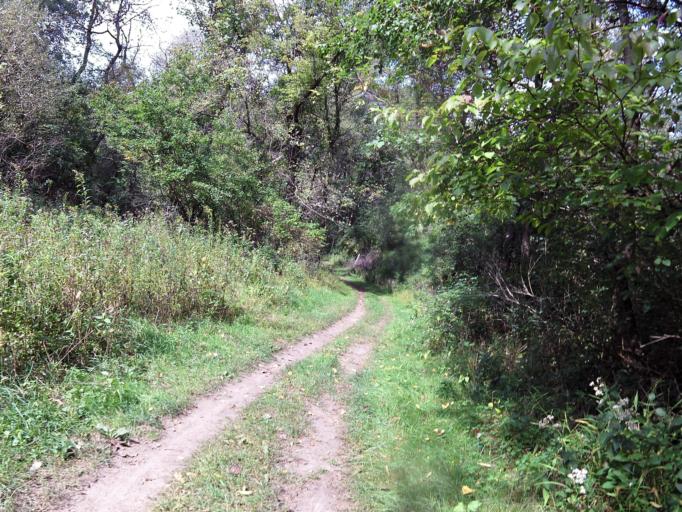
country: US
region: Minnesota
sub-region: Washington County
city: Afton
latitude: 44.8641
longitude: -92.7980
